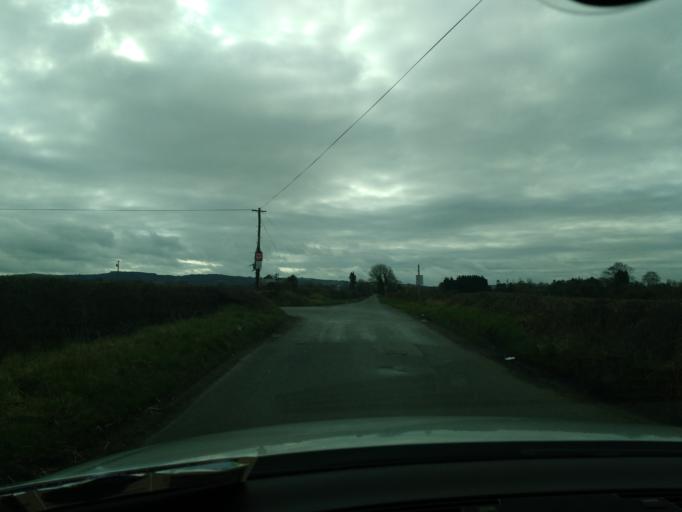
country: IE
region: Leinster
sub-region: Laois
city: Rathdowney
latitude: 52.7071
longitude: -7.5604
